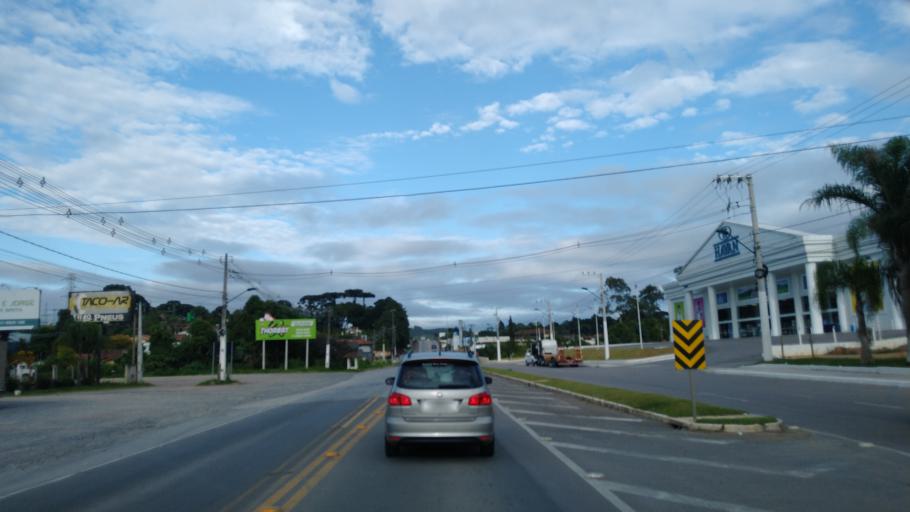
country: BR
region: Santa Catarina
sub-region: Sao Bento Do Sul
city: Sao Bento do Sul
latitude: -26.2239
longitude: -49.3979
